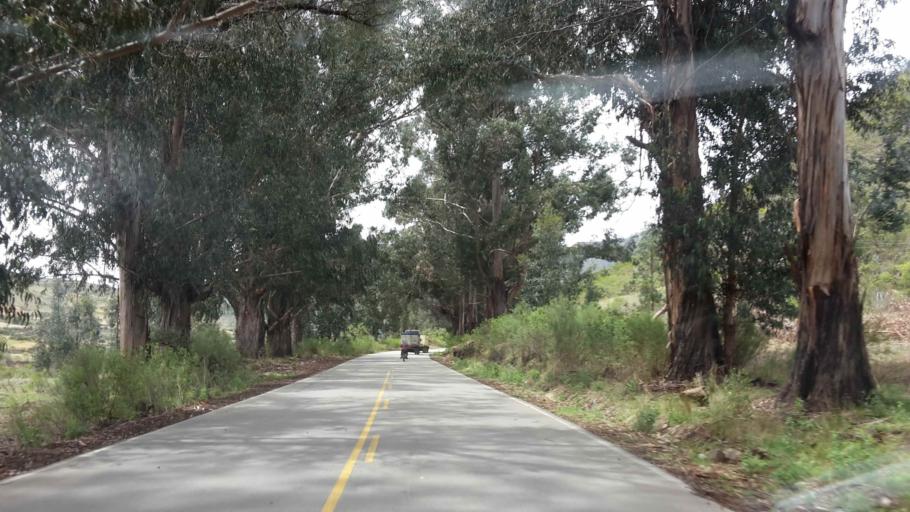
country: BO
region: Cochabamba
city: Totora
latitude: -17.6548
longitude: -65.2279
